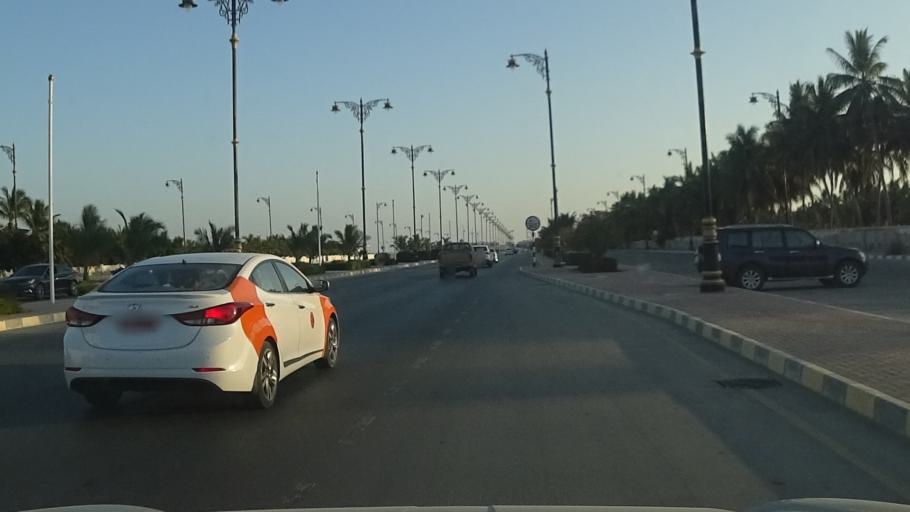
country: OM
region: Zufar
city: Salalah
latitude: 17.0342
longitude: 54.1720
